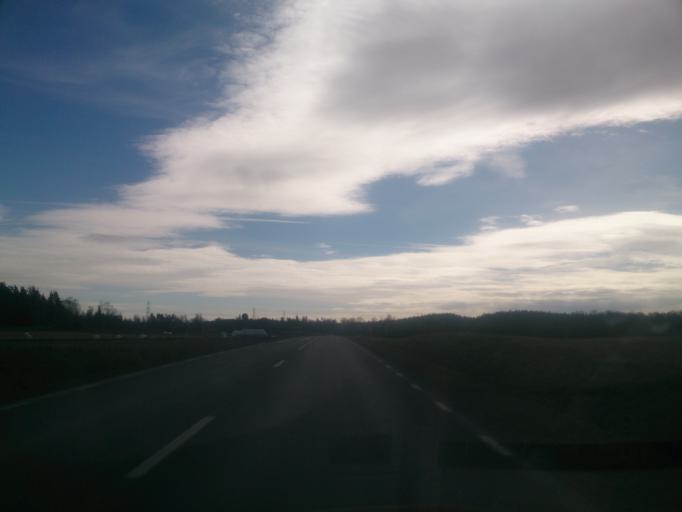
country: SE
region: OEstergoetland
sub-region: Norrkopings Kommun
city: Skarblacka
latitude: 58.6013
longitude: 15.8296
